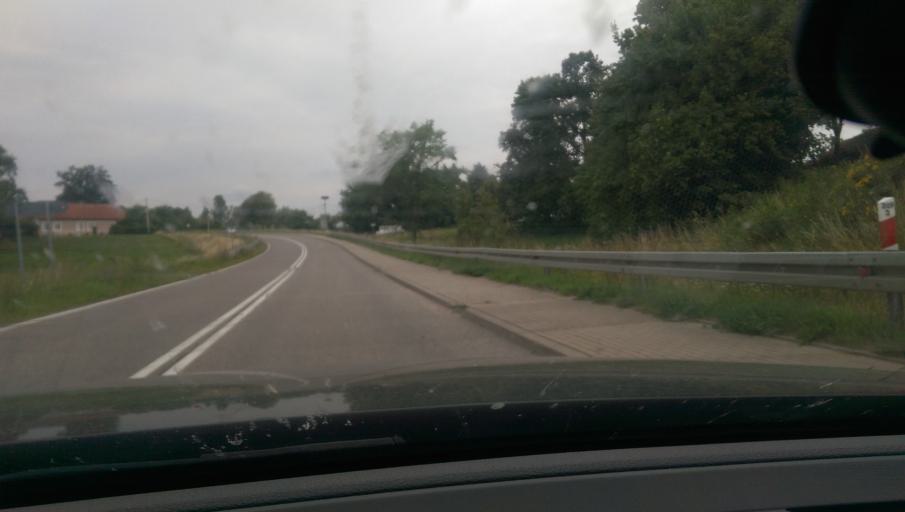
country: PL
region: Podlasie
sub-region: Powiat grajewski
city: Rajgrod
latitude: 53.8605
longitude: 22.5738
